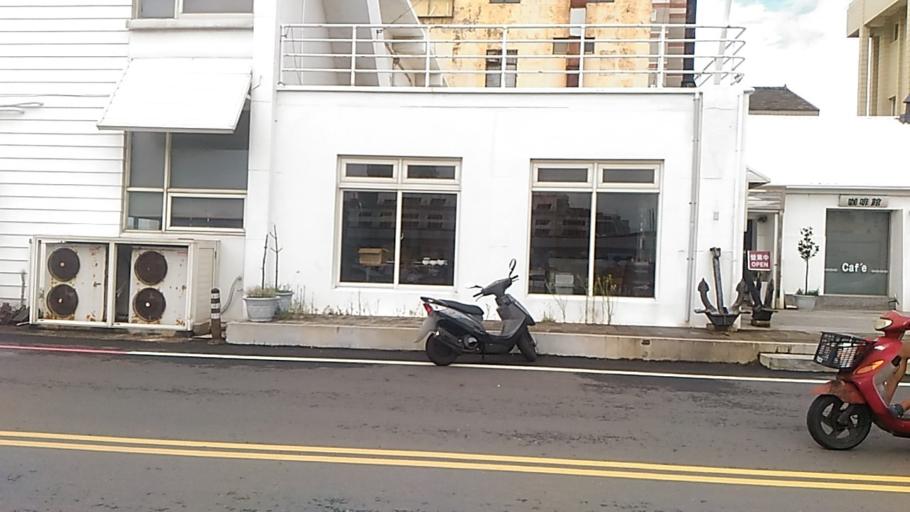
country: TW
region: Taiwan
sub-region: Penghu
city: Ma-kung
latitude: 23.5650
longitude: 119.5691
